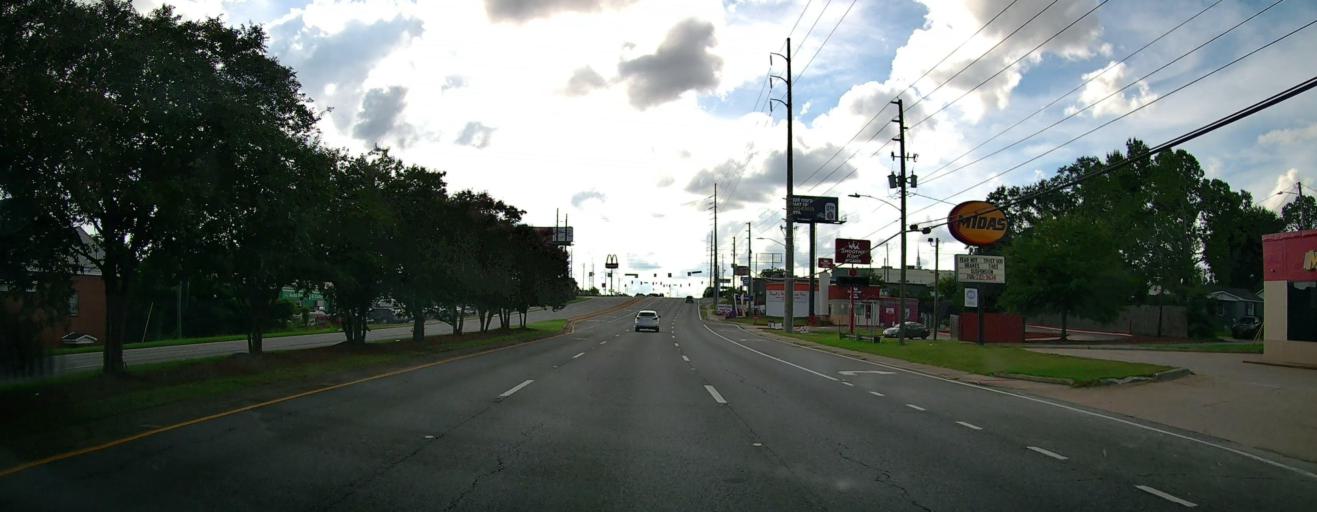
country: US
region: Alabama
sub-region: Russell County
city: Phenix City
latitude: 32.5071
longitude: -84.9678
